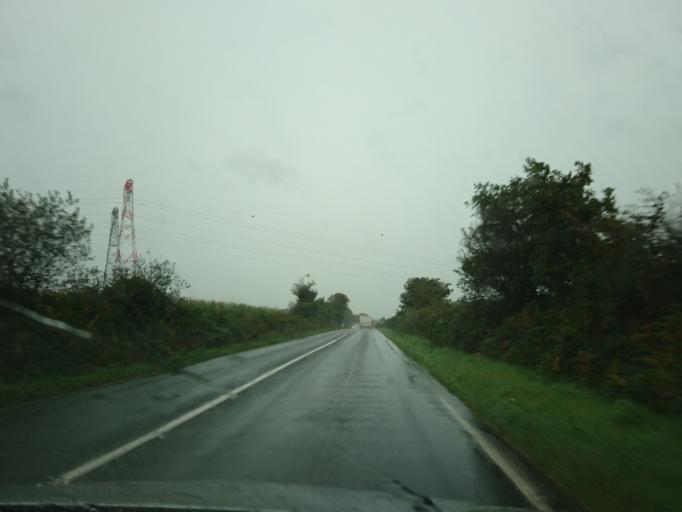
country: FR
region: Brittany
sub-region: Departement du Finistere
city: Plabennec
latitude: 48.4812
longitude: -4.4366
